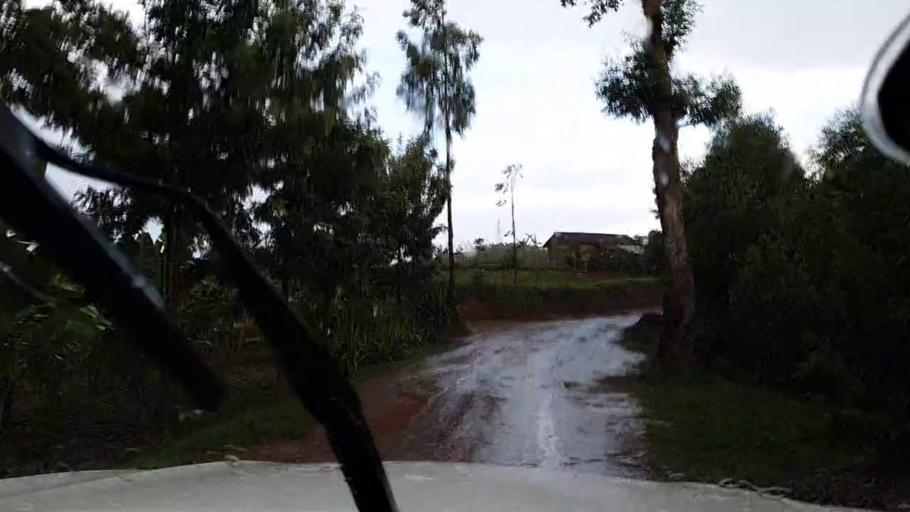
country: BI
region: Kayanza
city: Kayanza
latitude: -2.7726
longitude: 29.5448
